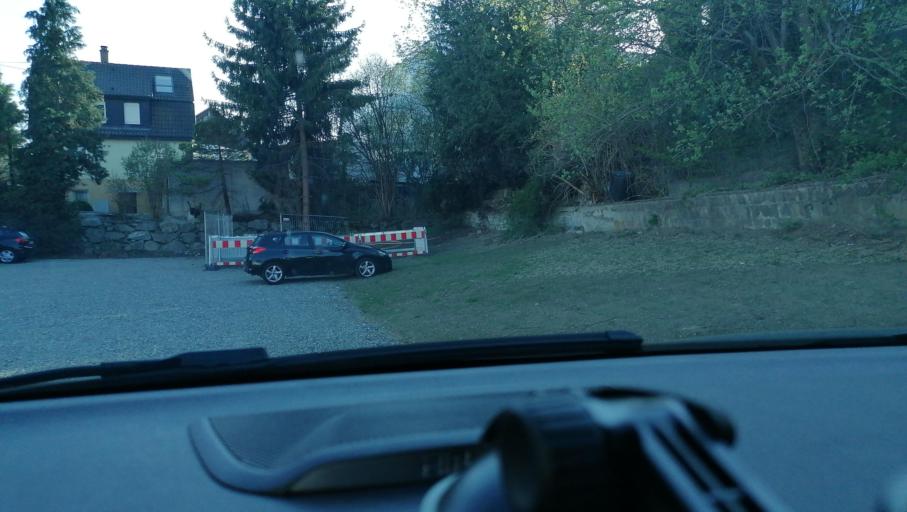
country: DE
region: Baden-Wuerttemberg
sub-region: Tuebingen Region
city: Aulendorf
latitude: 47.9520
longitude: 9.6368
